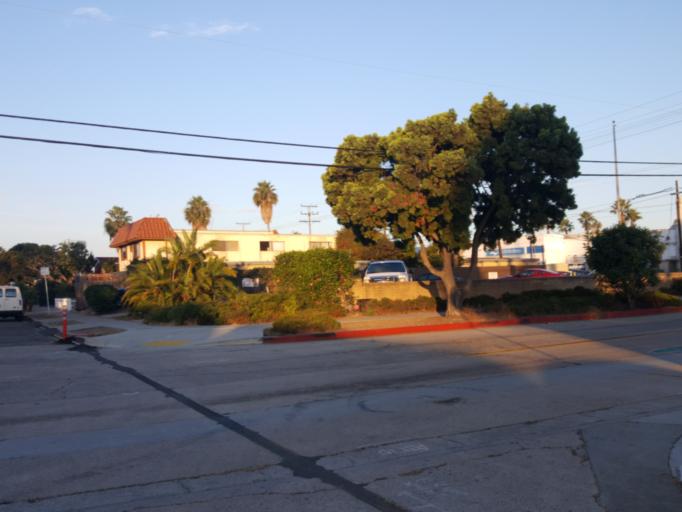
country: US
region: California
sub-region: San Diego County
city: La Jolla
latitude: 32.7977
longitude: -117.2459
